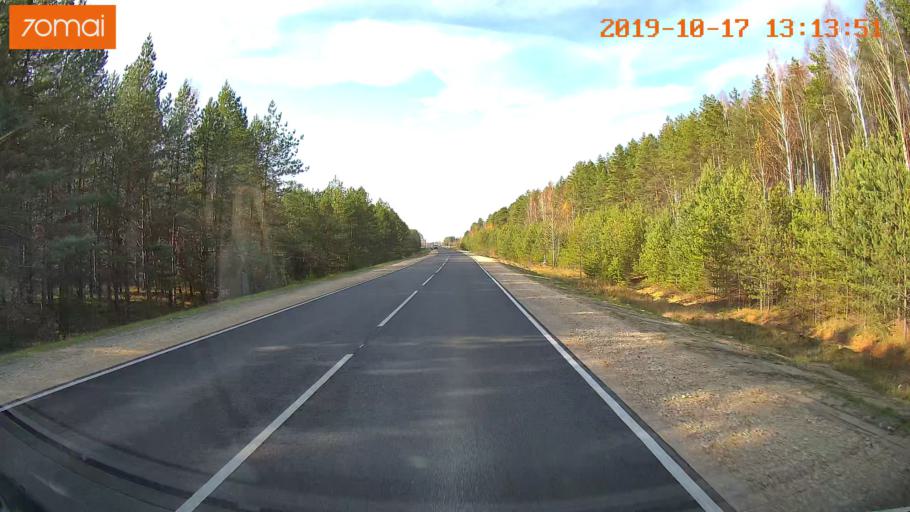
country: RU
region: Rjazan
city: Gus'-Zheleznyy
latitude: 55.0483
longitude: 41.1827
